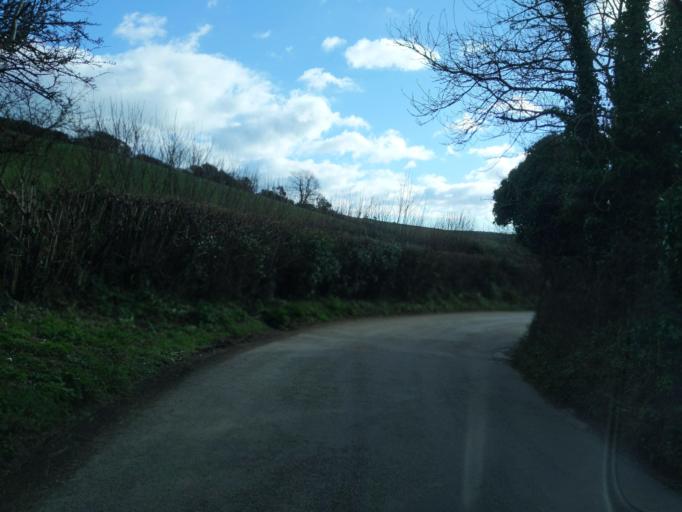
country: GB
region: England
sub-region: Devon
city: Salcombe
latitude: 50.2562
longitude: -3.7042
